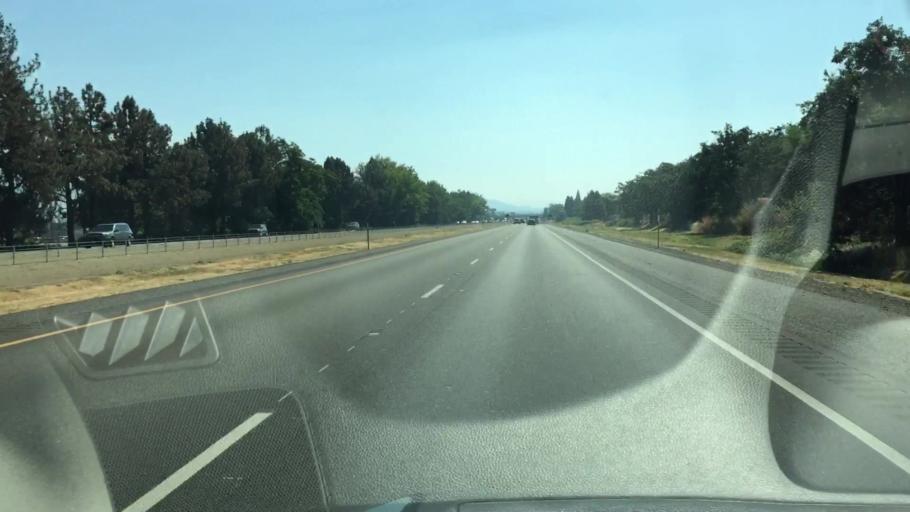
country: US
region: Oregon
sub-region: Jackson County
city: Central Point
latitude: 42.3864
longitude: -122.9150
